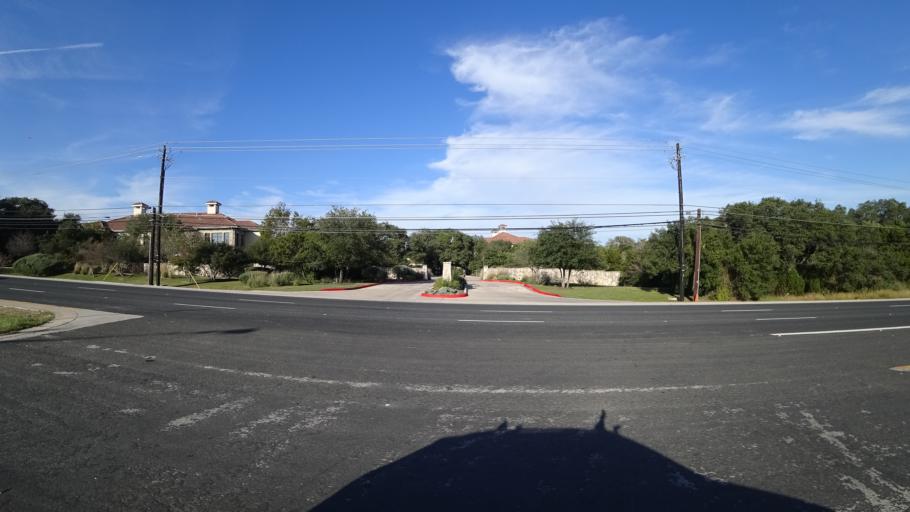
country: US
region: Texas
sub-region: Travis County
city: Barton Creek
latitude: 30.2473
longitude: -97.8483
